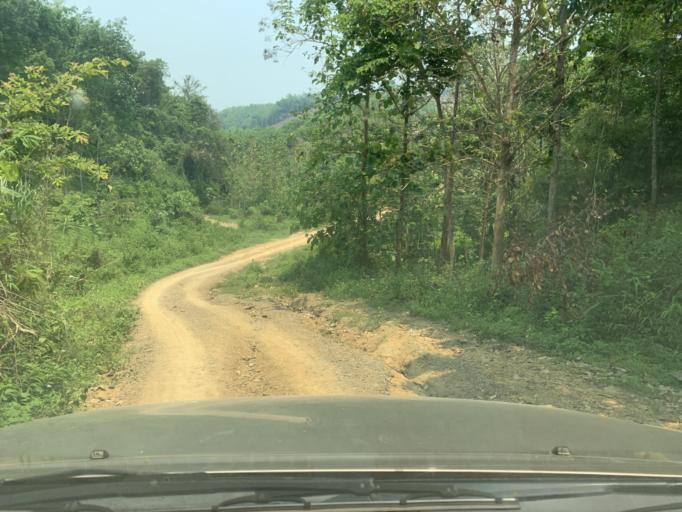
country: LA
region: Louangphabang
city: Xiang Ngeun
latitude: 19.8327
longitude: 102.2242
